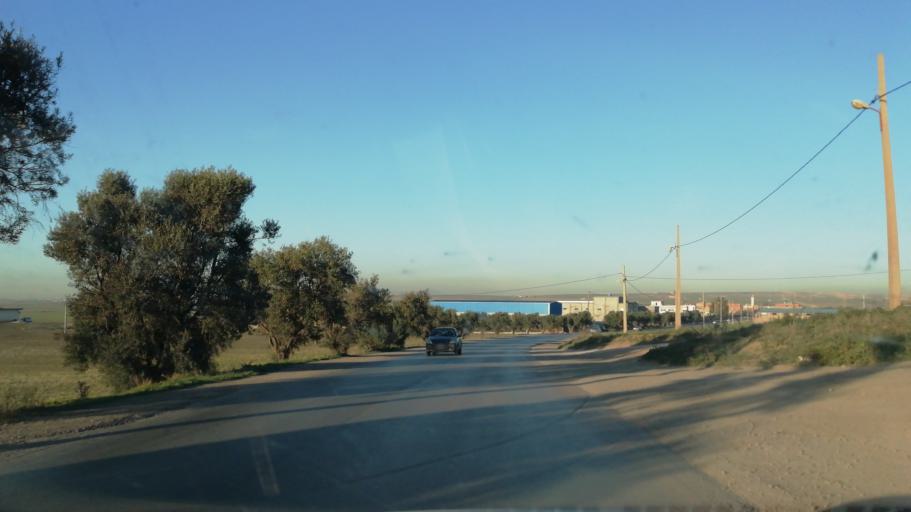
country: DZ
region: Oran
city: Es Senia
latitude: 35.5555
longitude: -0.5720
